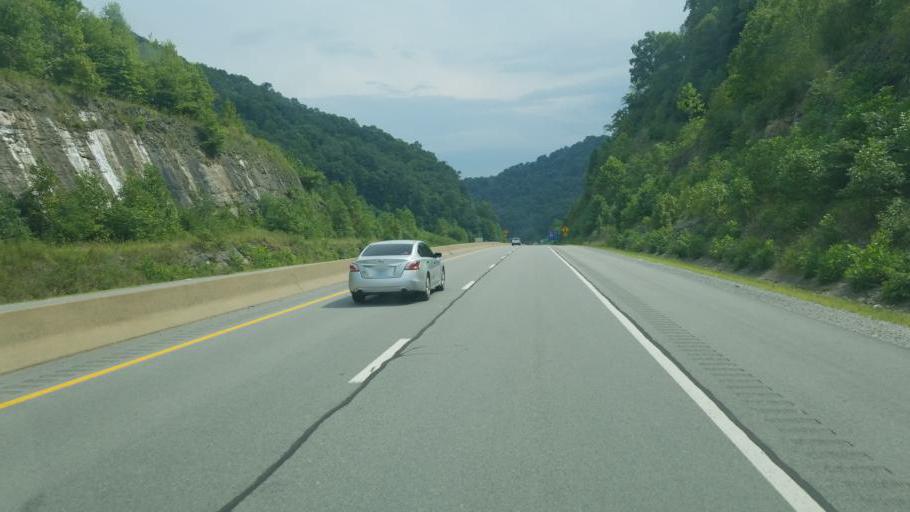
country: US
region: West Virginia
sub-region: Logan County
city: Mount Gay-Shamrock
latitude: 37.8706
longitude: -82.0460
